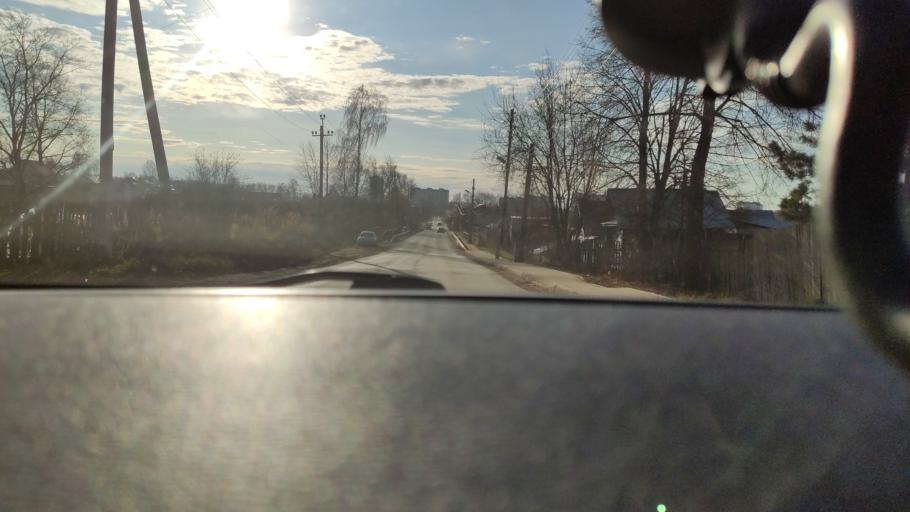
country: RU
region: Perm
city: Kondratovo
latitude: 58.0518
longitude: 56.0290
